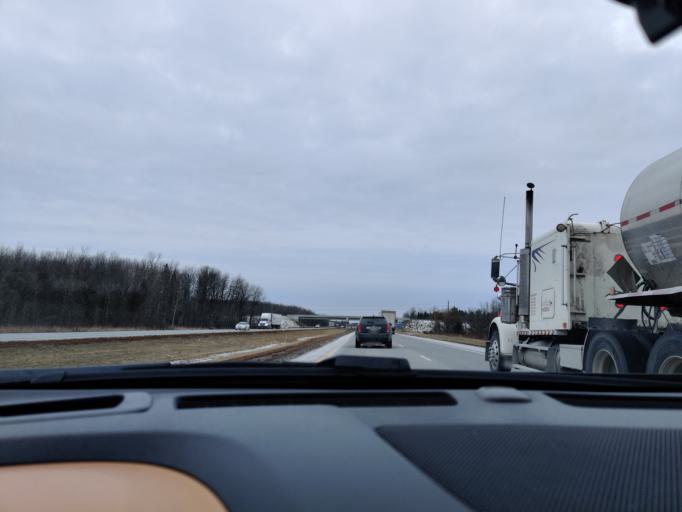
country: US
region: New York
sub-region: St. Lawrence County
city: Ogdensburg
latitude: 44.8719
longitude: -75.3027
